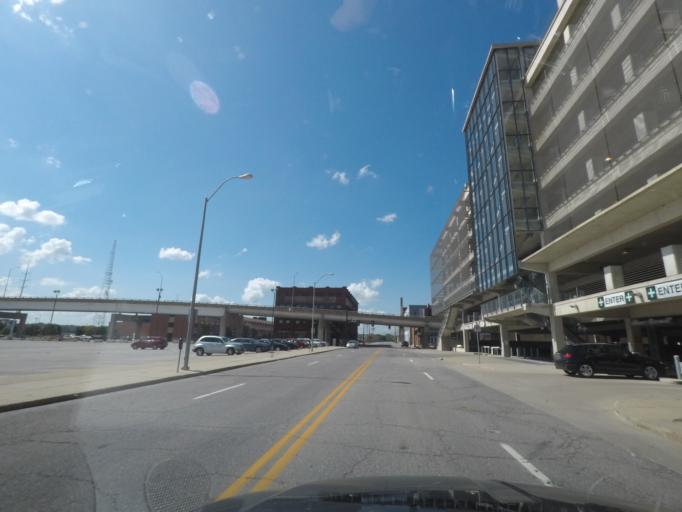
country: US
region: Iowa
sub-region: Polk County
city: Des Moines
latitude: 41.5835
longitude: -93.6267
